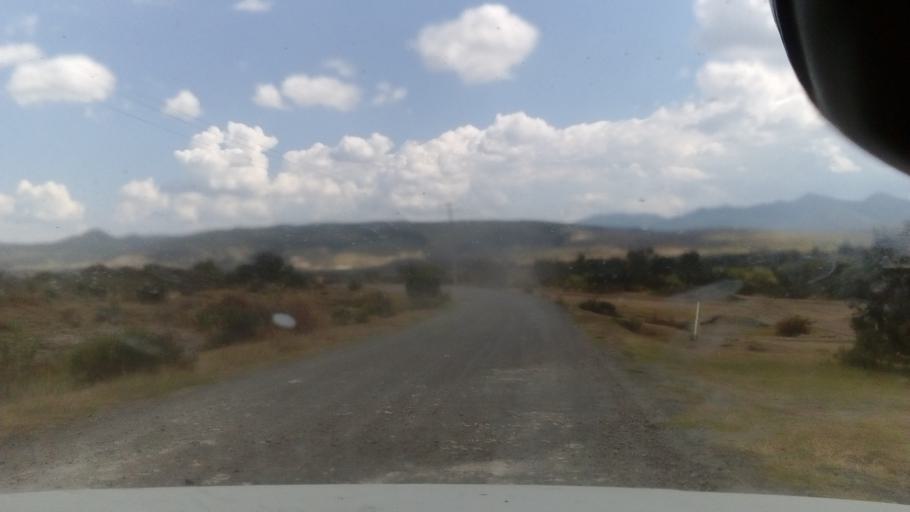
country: MX
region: Guanajuato
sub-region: Silao de la Victoria
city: San Francisco (Banos de Agua Caliente)
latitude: 21.1991
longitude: -101.4447
